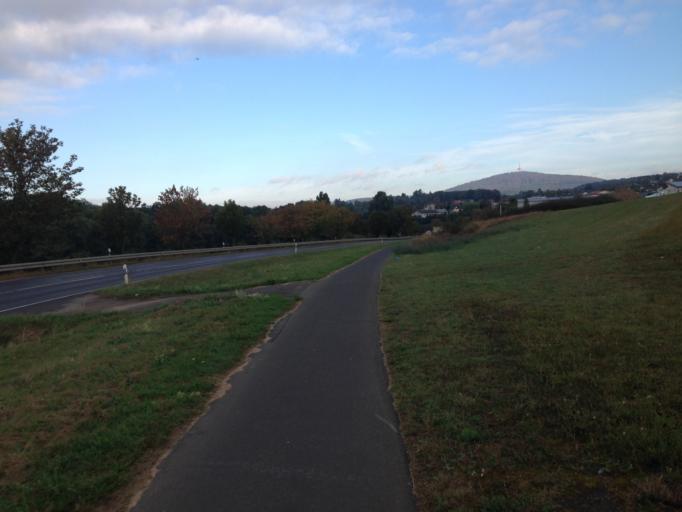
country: DE
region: Hesse
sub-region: Regierungsbezirk Giessen
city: Heuchelheim
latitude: 50.6094
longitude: 8.6152
